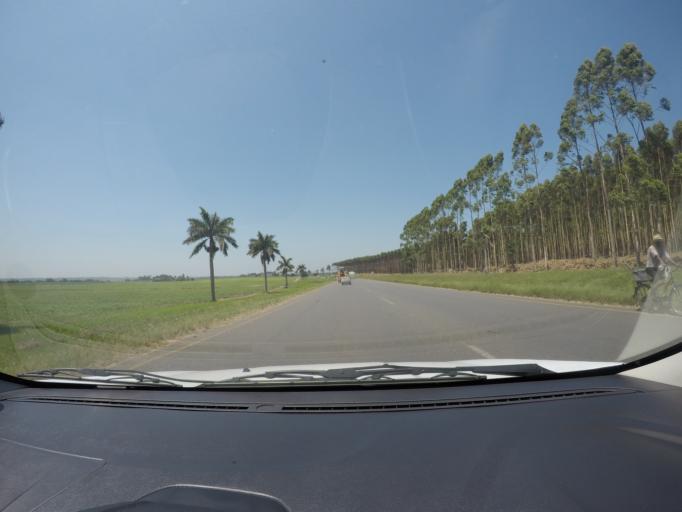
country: ZA
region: KwaZulu-Natal
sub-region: uThungulu District Municipality
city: eSikhawini
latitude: -28.8176
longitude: 31.9525
